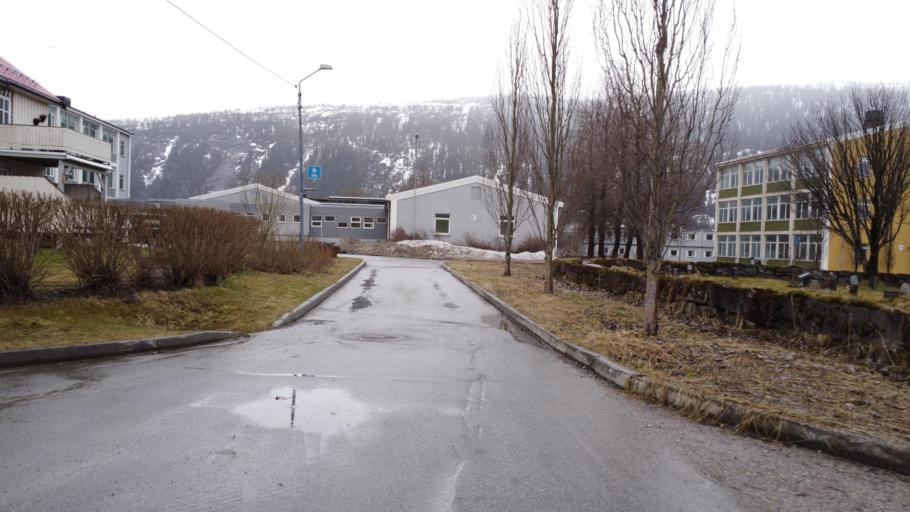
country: NO
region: Nordland
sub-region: Rana
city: Mo i Rana
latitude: 66.3098
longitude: 14.1472
